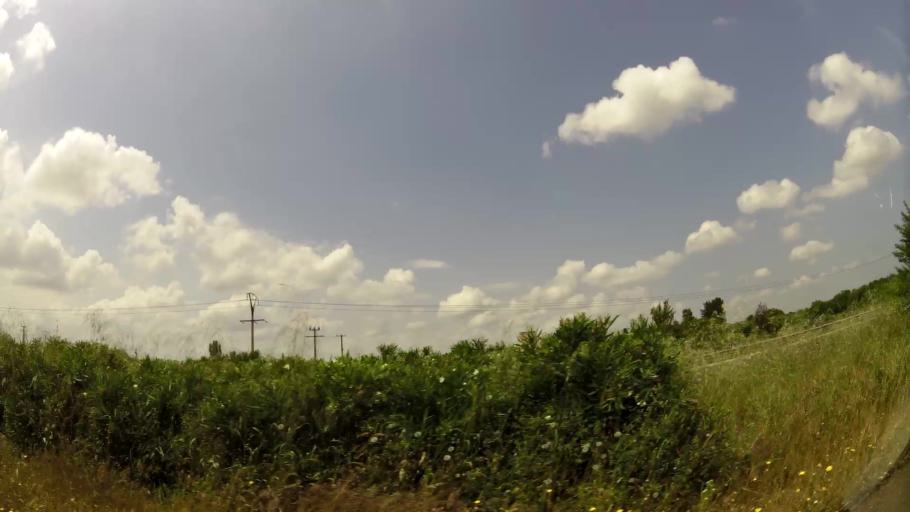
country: MA
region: Rabat-Sale-Zemmour-Zaer
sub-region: Khemisset
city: Tiflet
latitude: 33.9861
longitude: -6.5341
